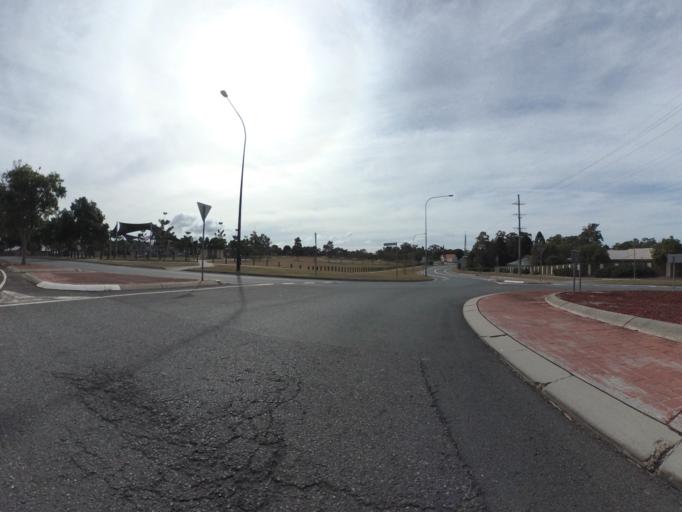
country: AU
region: Queensland
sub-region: Brisbane
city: Moggill
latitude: -27.5715
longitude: 152.8731
